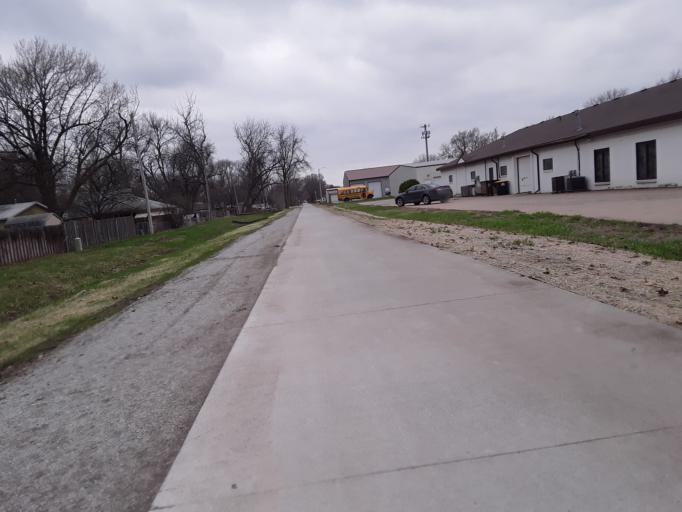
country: US
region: Nebraska
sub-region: Lancaster County
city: Lincoln
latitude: 40.8513
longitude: -96.6252
